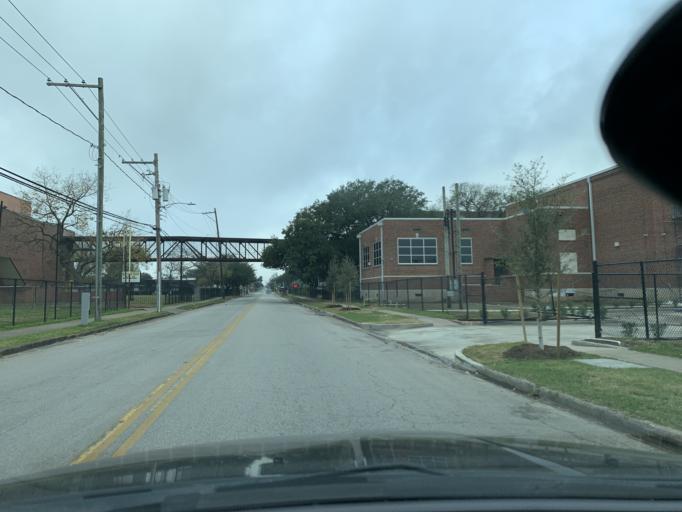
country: US
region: Texas
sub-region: Harris County
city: Houston
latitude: 29.7834
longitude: -95.3569
